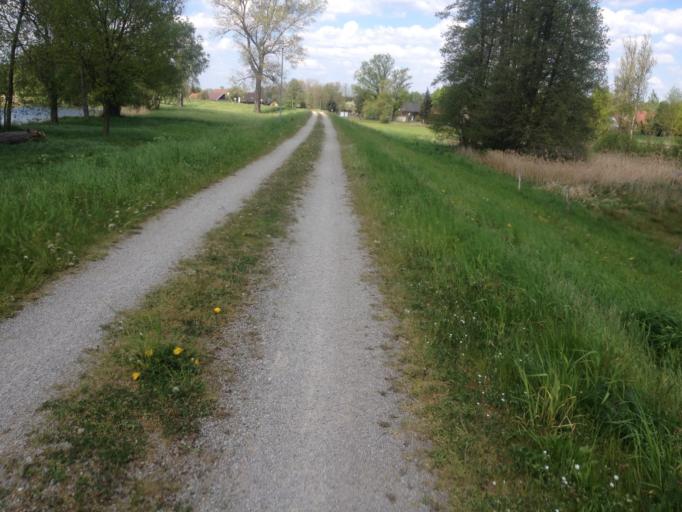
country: DE
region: Brandenburg
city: Drehnow
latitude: 51.8460
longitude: 14.3340
